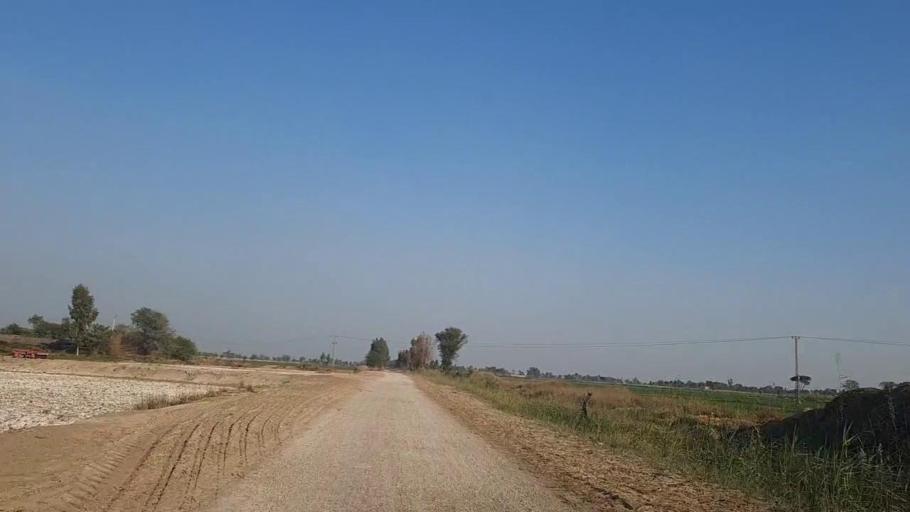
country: PK
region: Sindh
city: Daur
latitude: 26.3401
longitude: 68.1483
